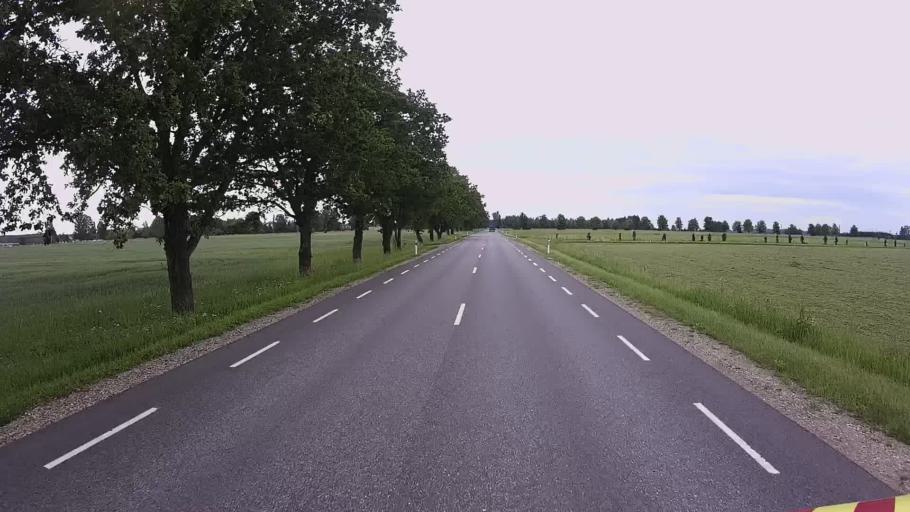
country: EE
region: Viljandimaa
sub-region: Karksi vald
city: Karksi-Nuia
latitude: 58.1291
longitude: 25.5824
